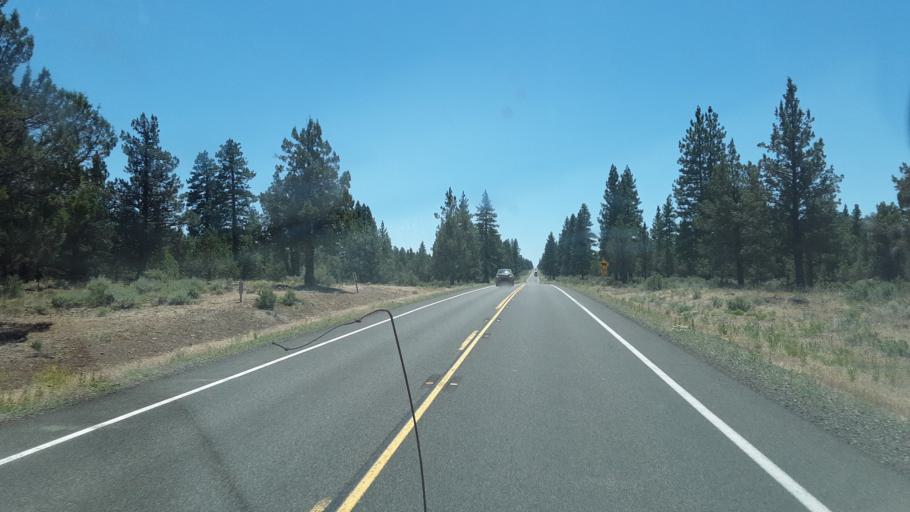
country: US
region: California
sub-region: Siskiyou County
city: Tulelake
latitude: 41.6295
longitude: -121.2262
